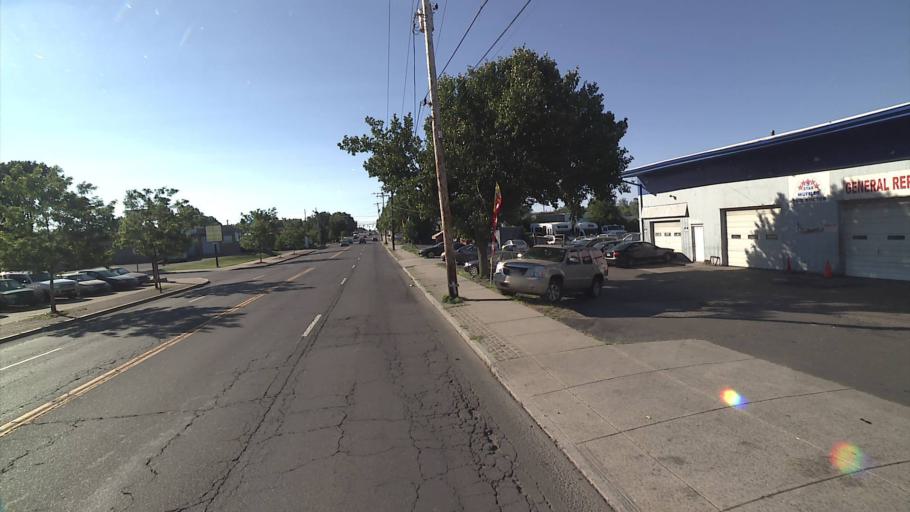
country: US
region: Connecticut
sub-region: New Haven County
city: New Haven
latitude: 41.2928
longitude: -72.9437
